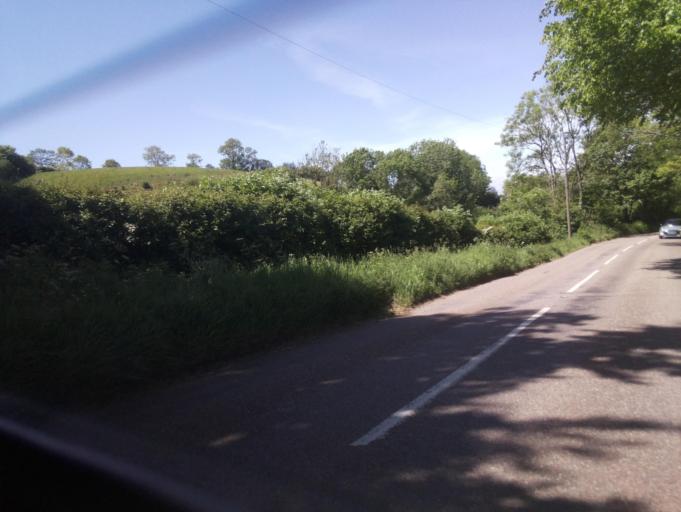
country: GB
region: England
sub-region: Devon
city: Newton Poppleford
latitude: 50.7124
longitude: -3.2720
